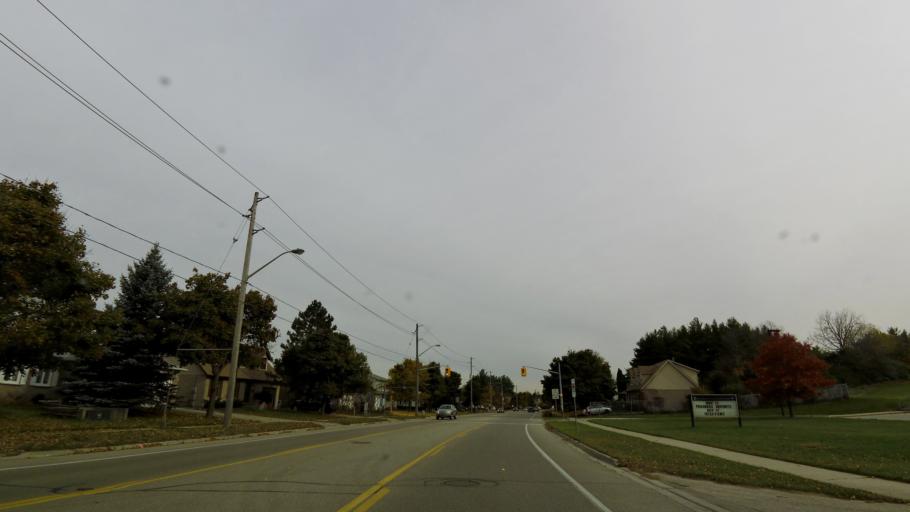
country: CA
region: Ontario
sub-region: Wellington County
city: Guelph
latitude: 43.5256
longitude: -80.2823
